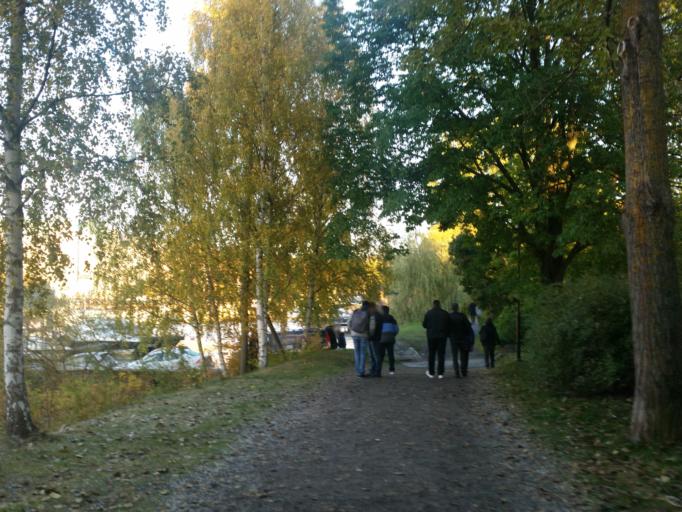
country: SE
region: Stockholm
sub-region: Stockholms Kommun
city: OEstermalm
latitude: 59.3305
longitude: 18.0906
